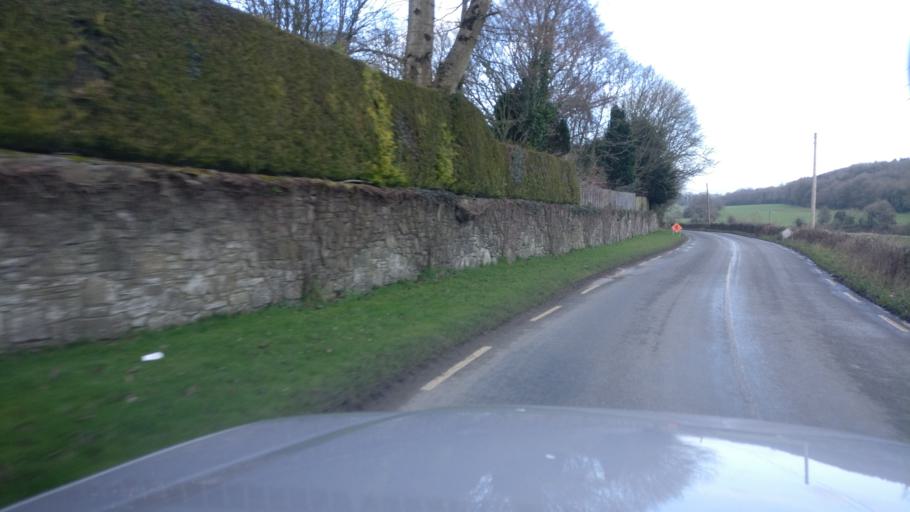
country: IE
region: Leinster
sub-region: Kilkenny
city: Castlecomer
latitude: 52.8161
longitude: -7.2140
